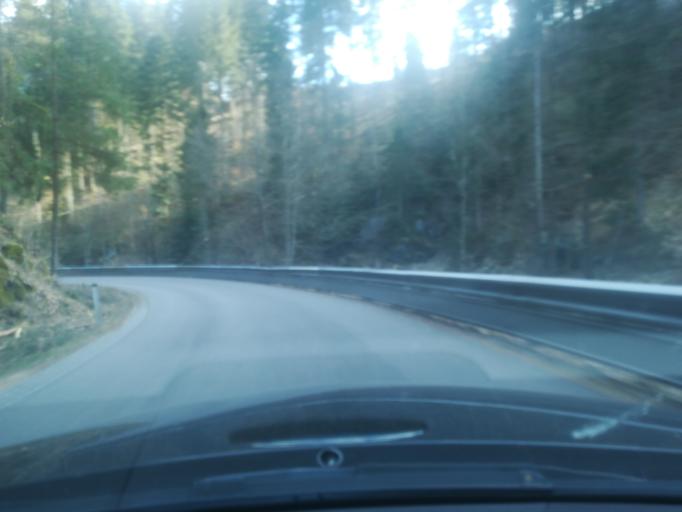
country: AT
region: Upper Austria
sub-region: Politischer Bezirk Freistadt
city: Freistadt
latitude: 48.4153
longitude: 14.6383
